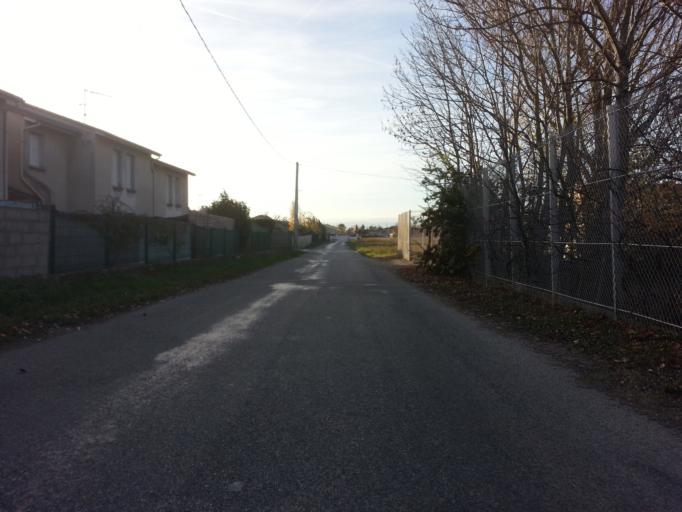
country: FR
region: Rhone-Alpes
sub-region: Departement de la Drome
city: Chabeuil
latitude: 44.9047
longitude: 5.0178
